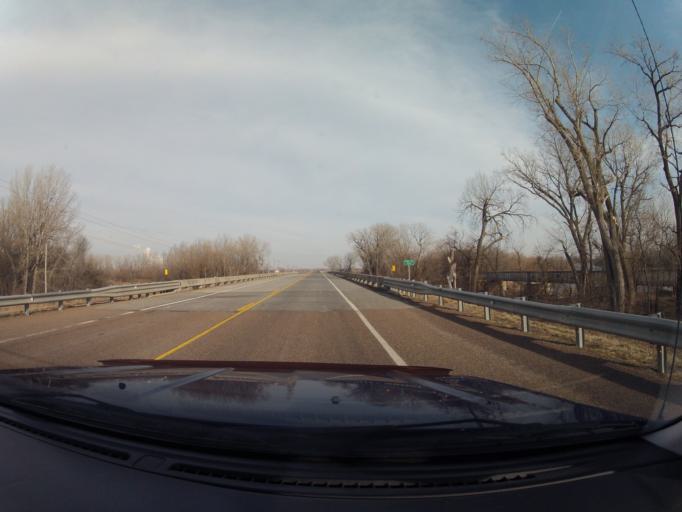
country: US
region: Kansas
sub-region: Pottawatomie County
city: Wamego
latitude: 39.2132
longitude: -96.2363
